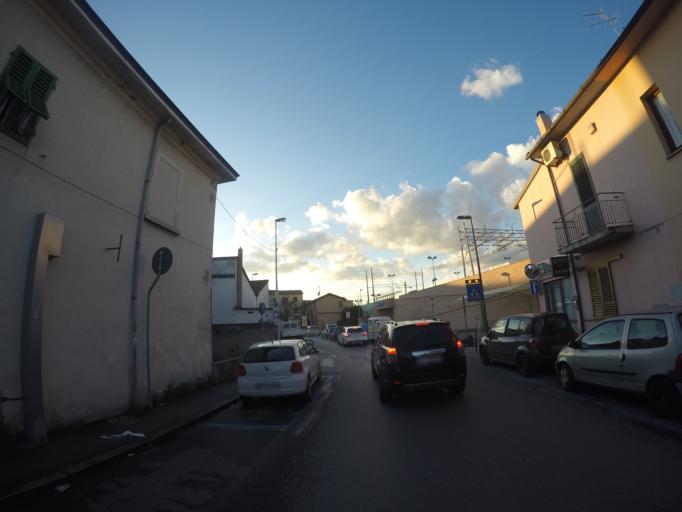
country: IT
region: Tuscany
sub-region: Provincia di Prato
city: Prato
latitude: 43.8910
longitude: 11.0760
